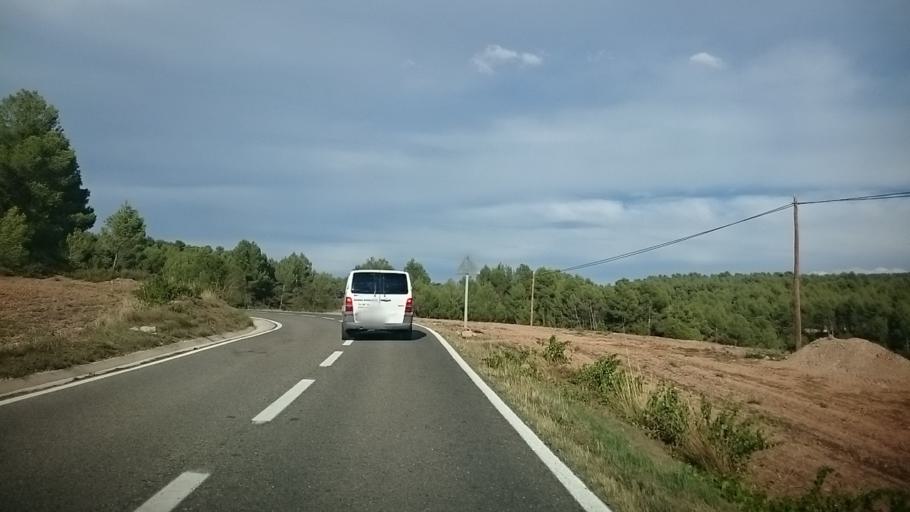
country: ES
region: Catalonia
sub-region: Provincia de Barcelona
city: Odena
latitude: 41.6160
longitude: 1.6502
